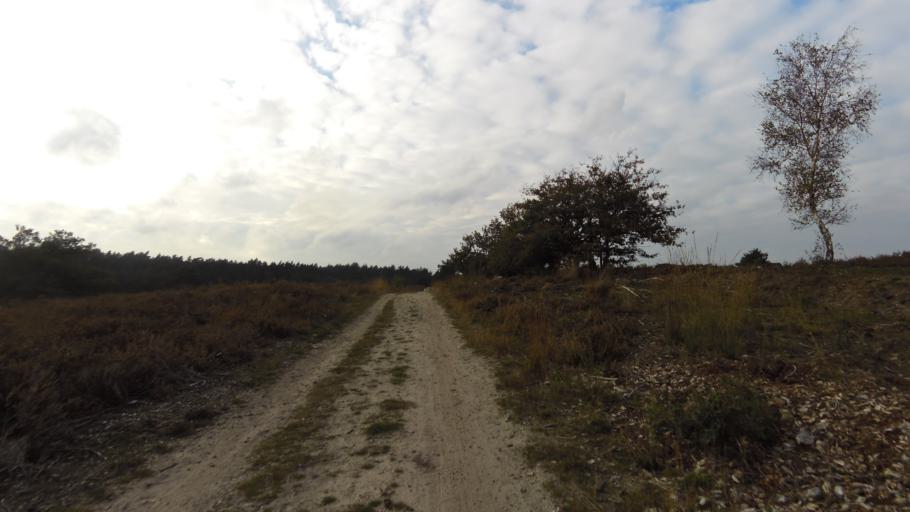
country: NL
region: Gelderland
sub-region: Gemeente Epe
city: Emst
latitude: 52.3249
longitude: 5.8841
